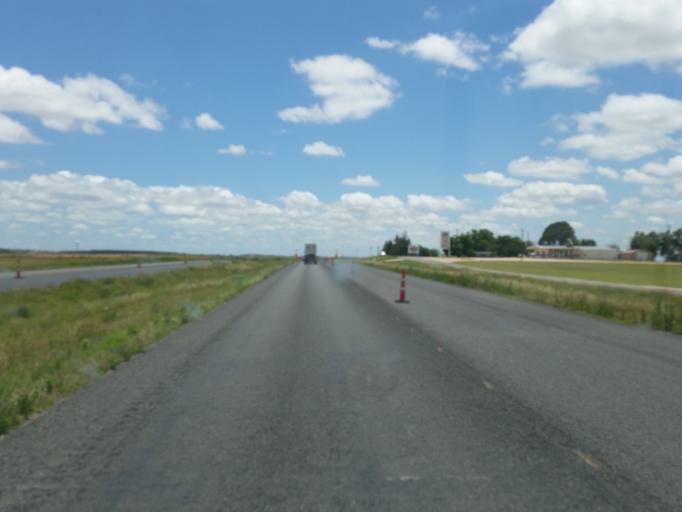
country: US
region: Texas
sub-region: Scurry County
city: Snyder
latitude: 32.7249
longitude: -100.8907
